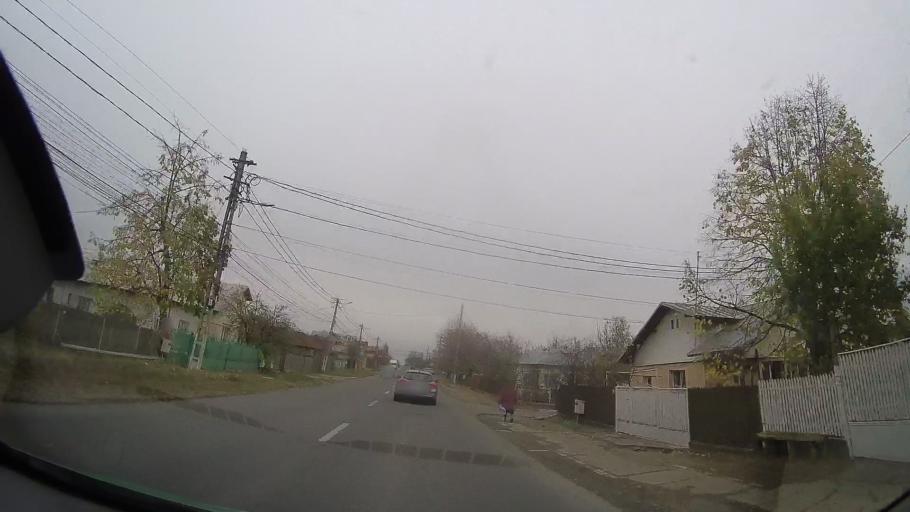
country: RO
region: Prahova
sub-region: Oras Baicoi
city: Tintea
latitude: 45.0315
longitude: 25.9123
